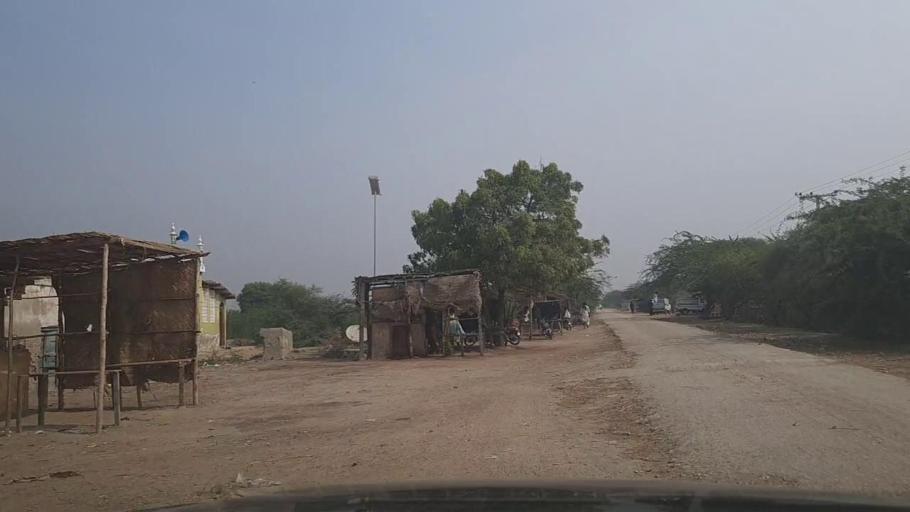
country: PK
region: Sindh
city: Mirpur Sakro
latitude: 24.4796
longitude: 67.6473
